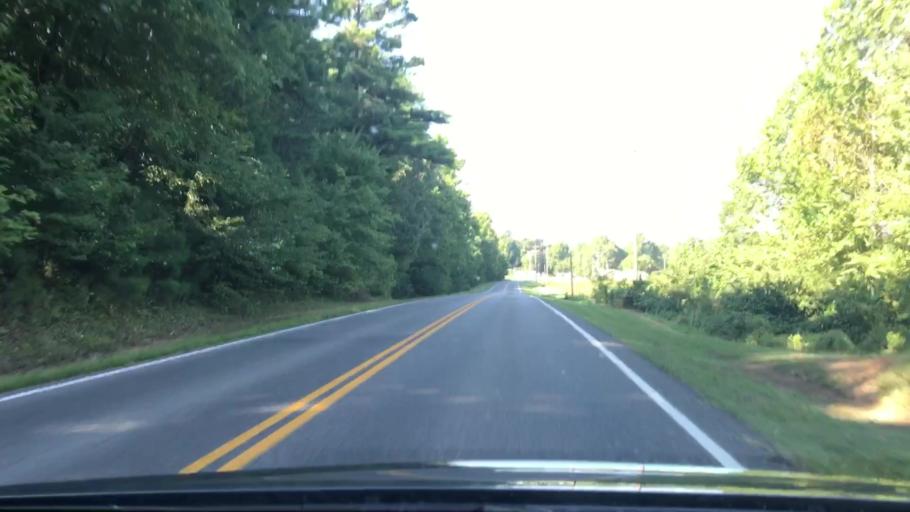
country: US
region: Kentucky
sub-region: Marshall County
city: Benton
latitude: 36.7769
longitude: -88.4781
